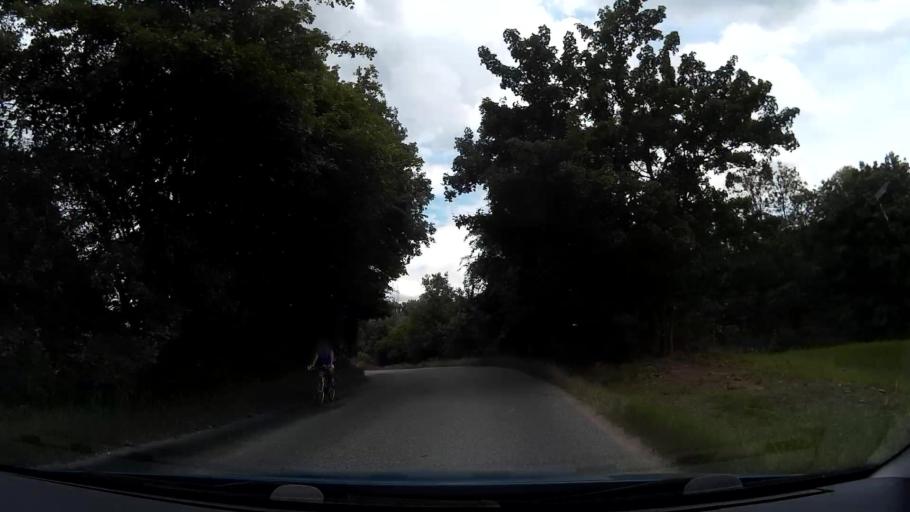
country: CZ
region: South Moravian
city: Ostopovice
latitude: 49.1419
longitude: 16.5317
